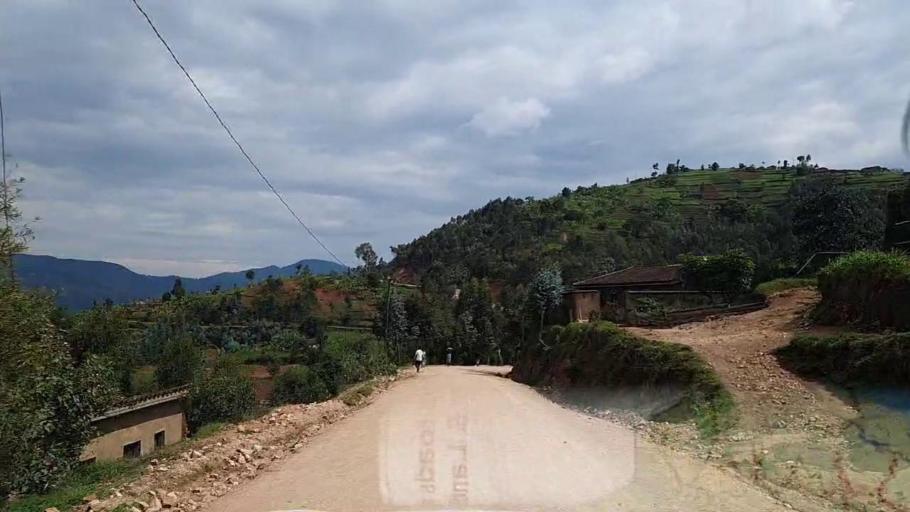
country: RW
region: Southern Province
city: Nzega
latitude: -2.3361
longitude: 29.4442
